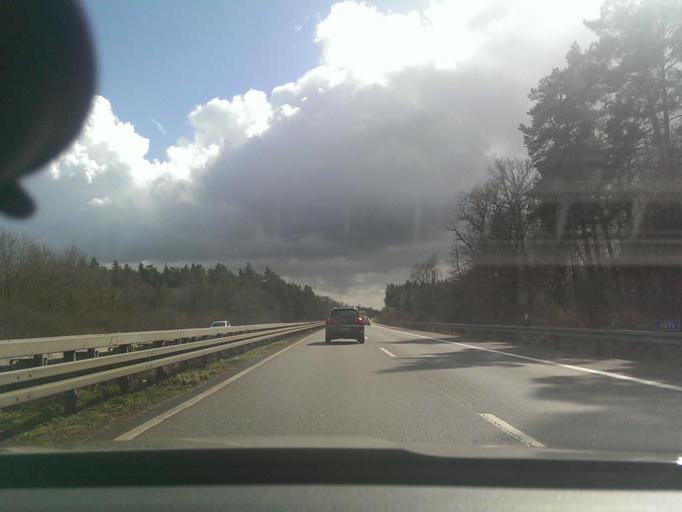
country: DE
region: Lower Saxony
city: Lehre
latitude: 52.3324
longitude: 10.7339
